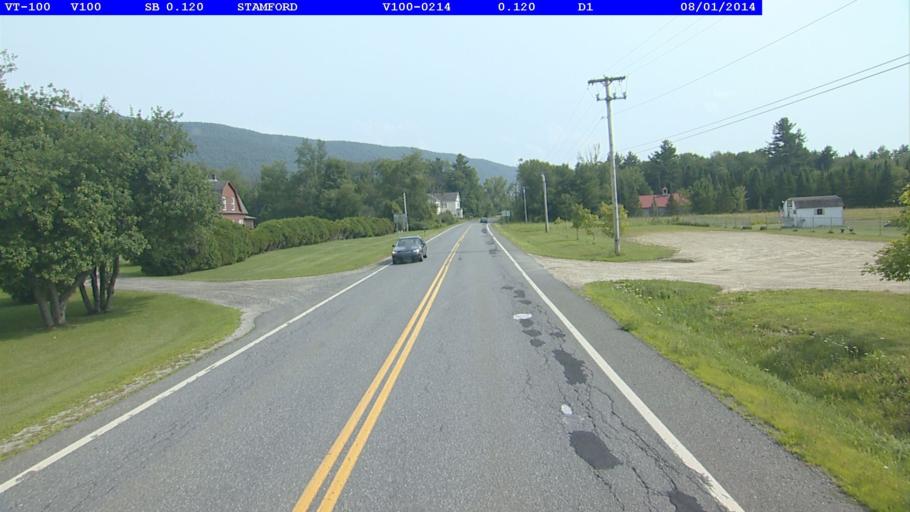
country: US
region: Massachusetts
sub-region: Berkshire County
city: North Adams
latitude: 42.7438
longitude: -73.0723
